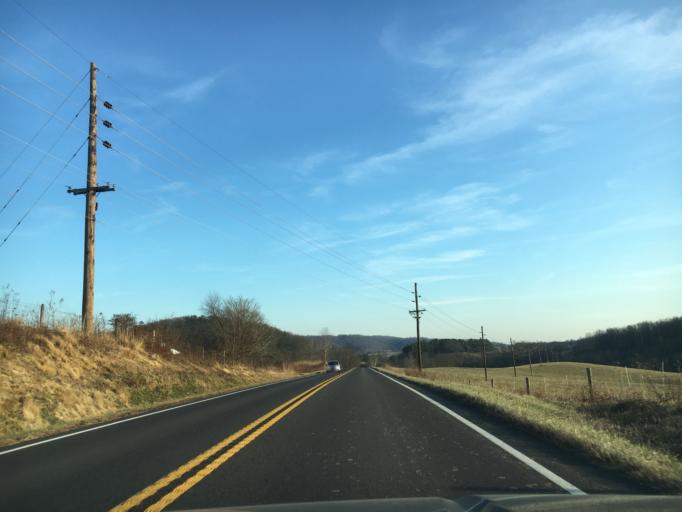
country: US
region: Virginia
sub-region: Rappahannock County
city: Washington
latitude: 38.6355
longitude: -78.1958
